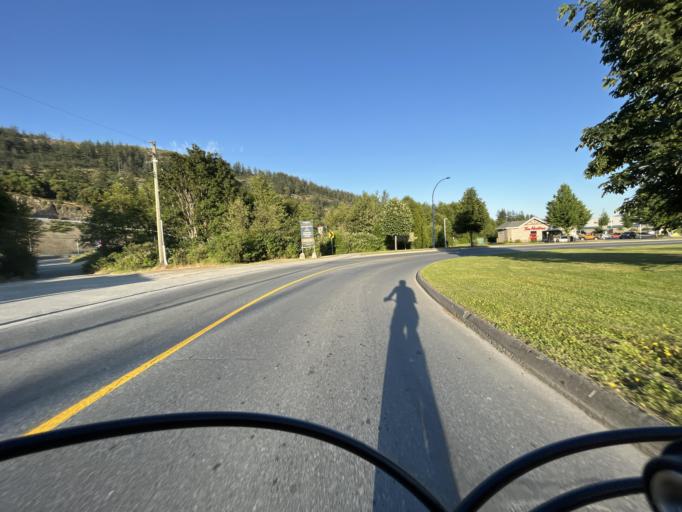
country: CA
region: British Columbia
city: Langford
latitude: 48.4578
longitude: -123.5409
